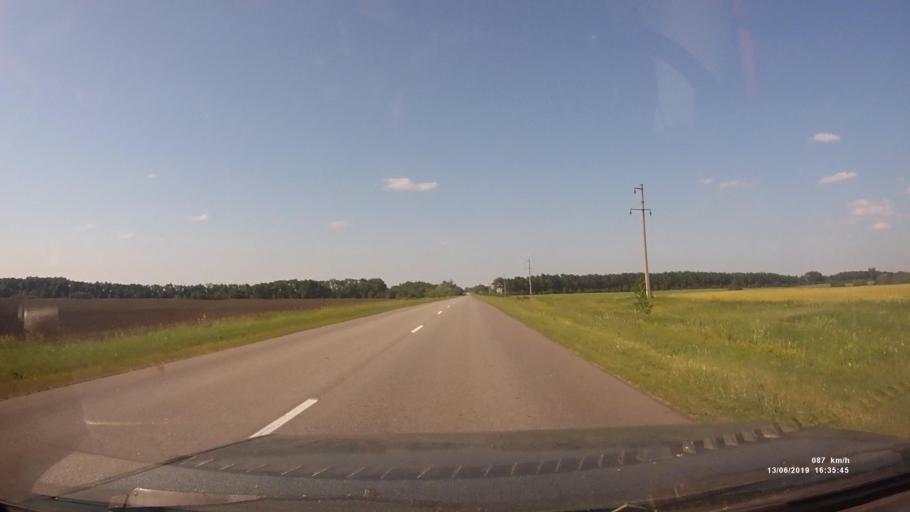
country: RU
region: Rostov
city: Kazanskaya
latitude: 49.8859
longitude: 41.3007
